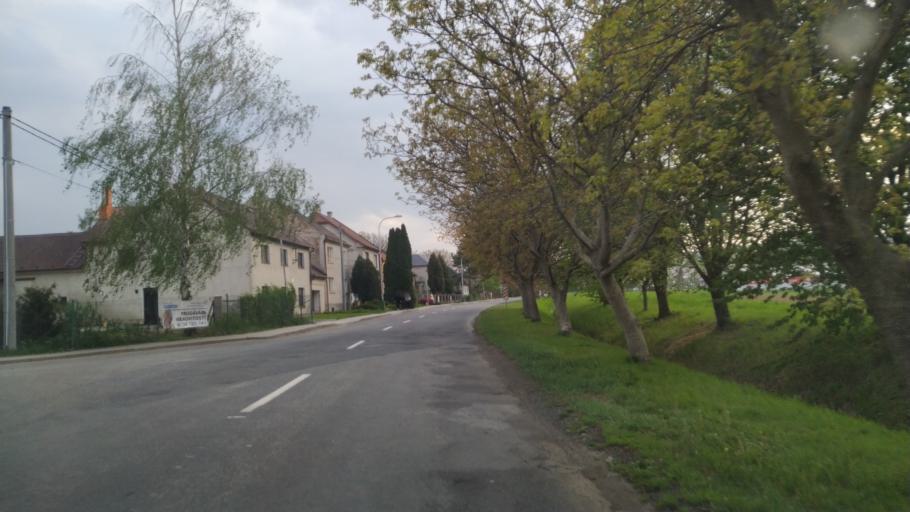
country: CZ
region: Olomoucky
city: Lutin
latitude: 49.5497
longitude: 17.1215
